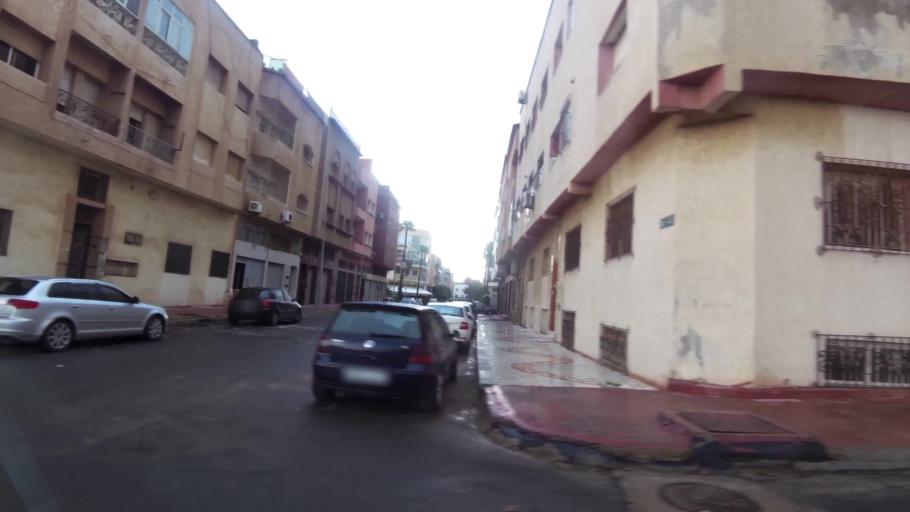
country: MA
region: Grand Casablanca
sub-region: Casablanca
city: Casablanca
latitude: 33.5362
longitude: -7.6805
